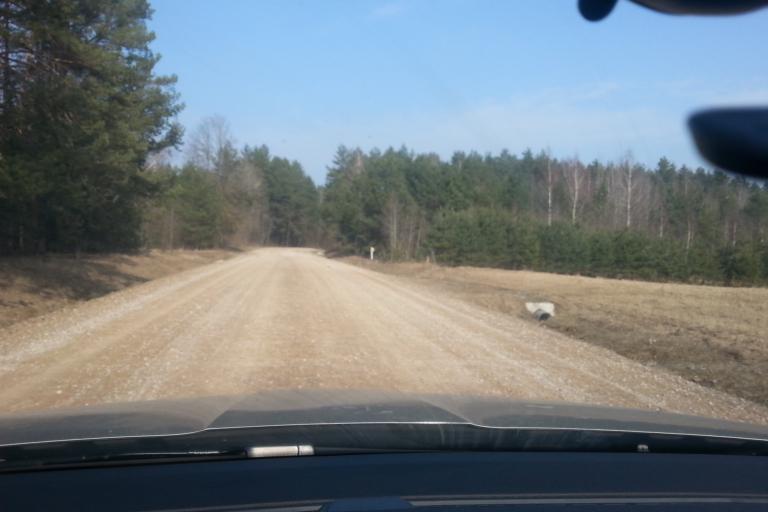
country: LT
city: Trakai
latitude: 54.5740
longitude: 24.9681
